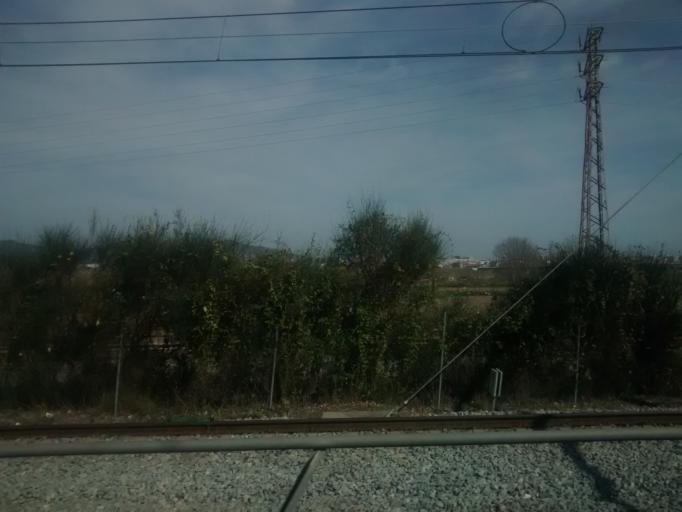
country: ES
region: Catalonia
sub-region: Provincia de Barcelona
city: Sant Boi de Llobregat
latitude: 41.3597
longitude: 2.0338
